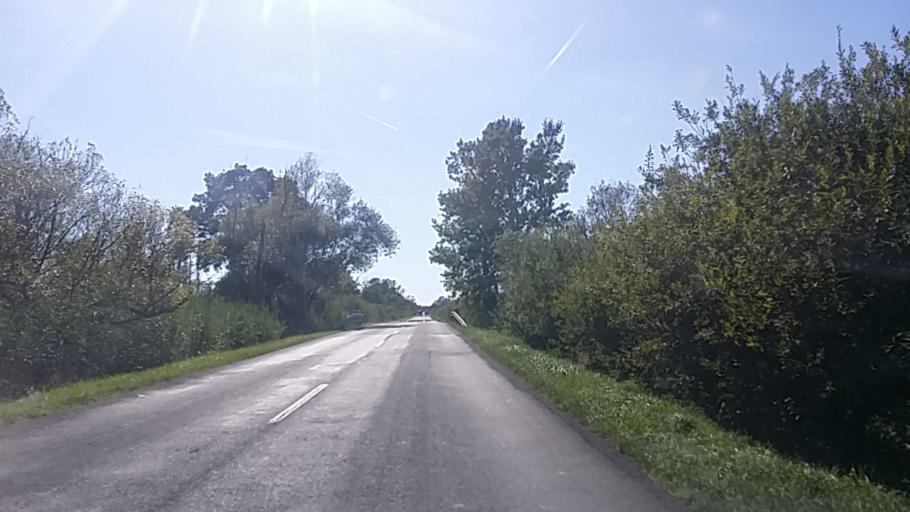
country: HU
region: Zala
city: Sarmellek
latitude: 46.7085
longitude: 17.2231
